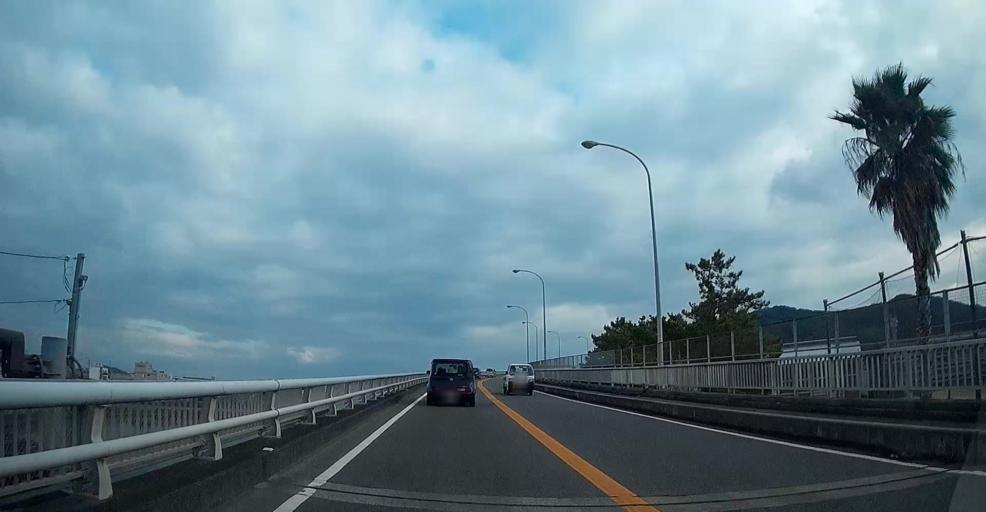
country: JP
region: Kumamoto
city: Hondo
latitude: 32.4473
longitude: 130.2008
